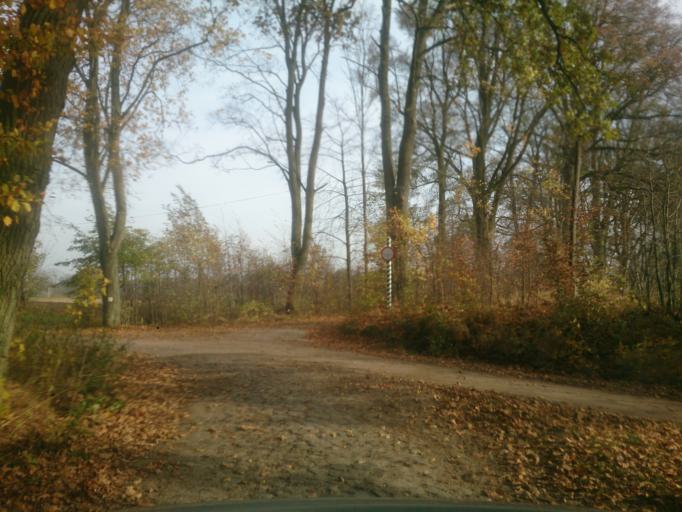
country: PL
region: Kujawsko-Pomorskie
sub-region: Powiat brodnicki
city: Brodnica
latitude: 53.3446
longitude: 19.3580
